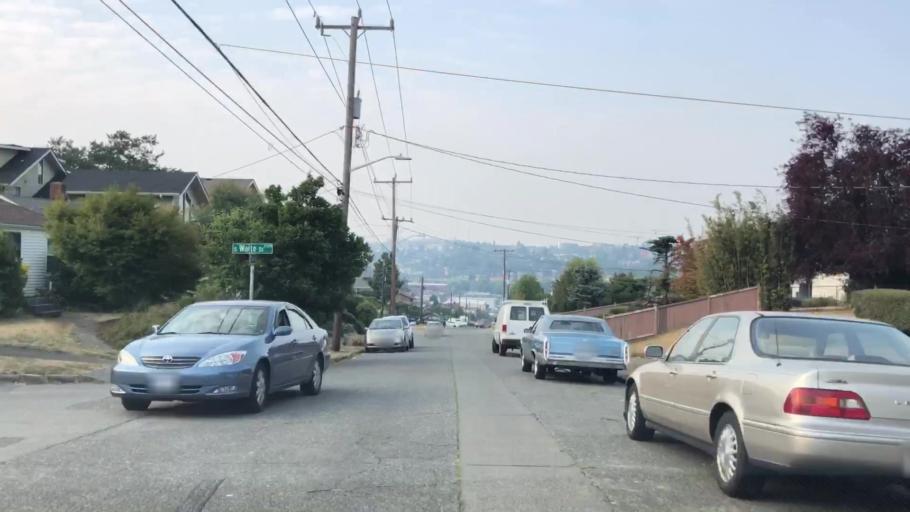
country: US
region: Washington
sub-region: King County
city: Seattle
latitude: 47.5800
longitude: -122.3054
